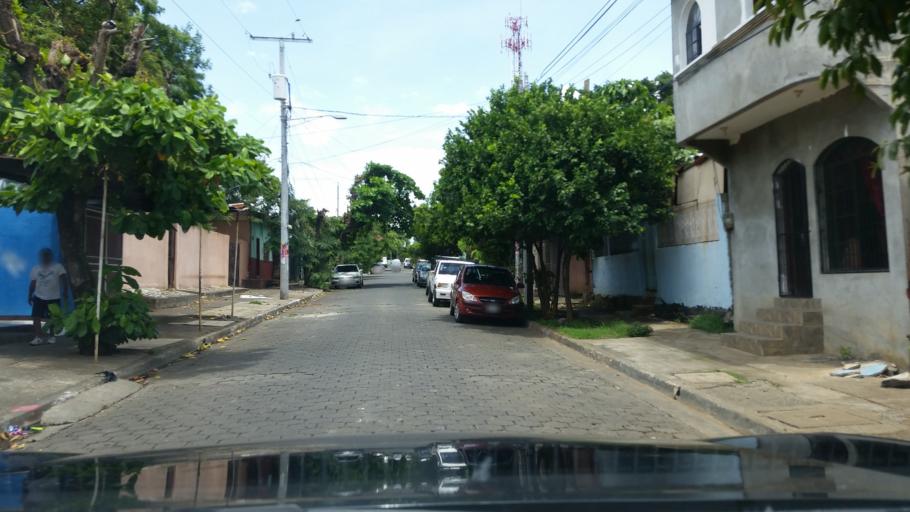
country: NI
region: Managua
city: Managua
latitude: 12.1289
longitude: -86.2576
